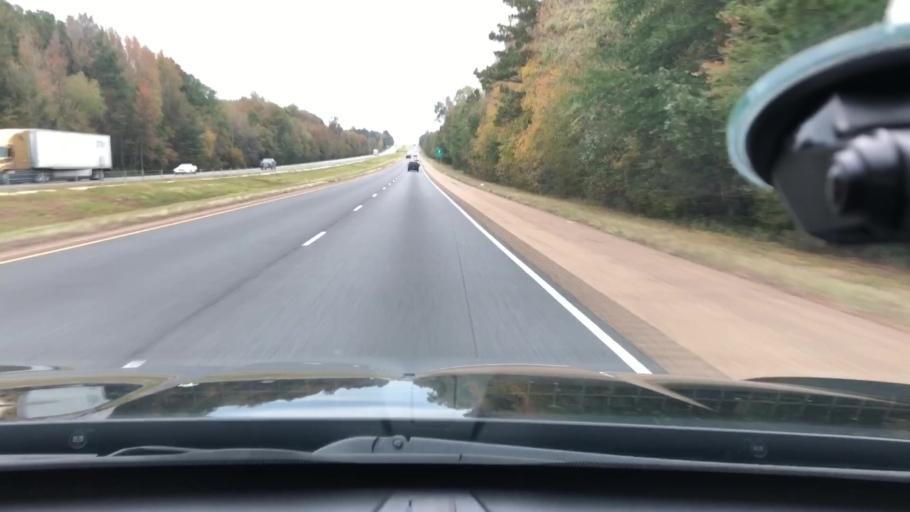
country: US
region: Arkansas
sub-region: Clark County
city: Gurdon
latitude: 33.9806
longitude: -93.1998
